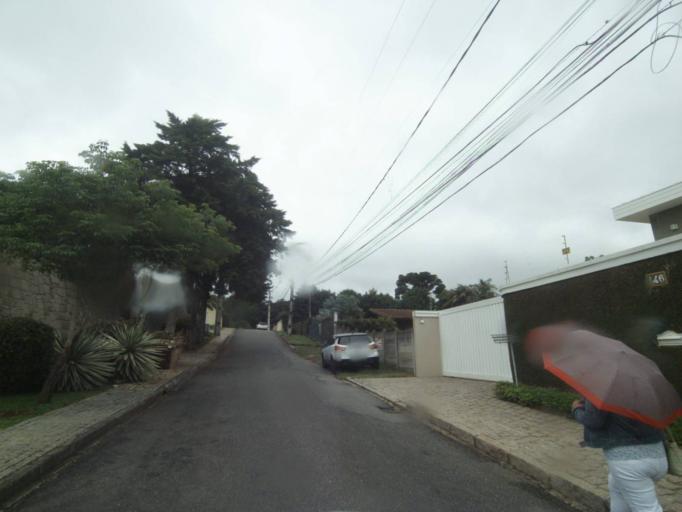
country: BR
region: Parana
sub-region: Curitiba
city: Curitiba
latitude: -25.4241
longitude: -49.3155
